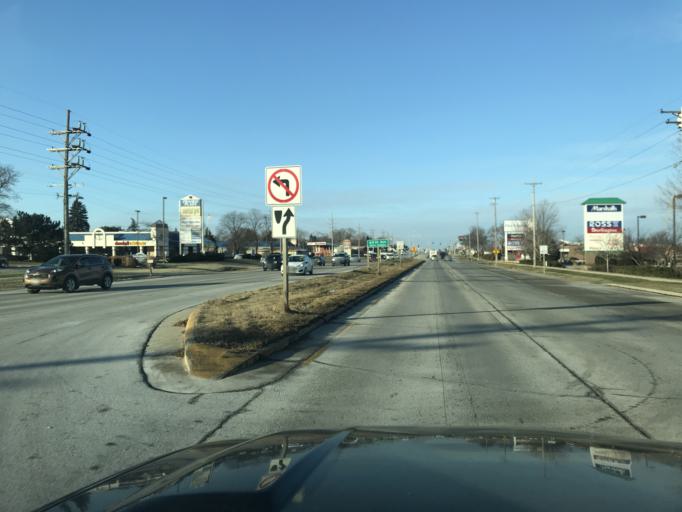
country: US
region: Wisconsin
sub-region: Kenosha County
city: Kenosha
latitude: 42.5665
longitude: -87.8762
